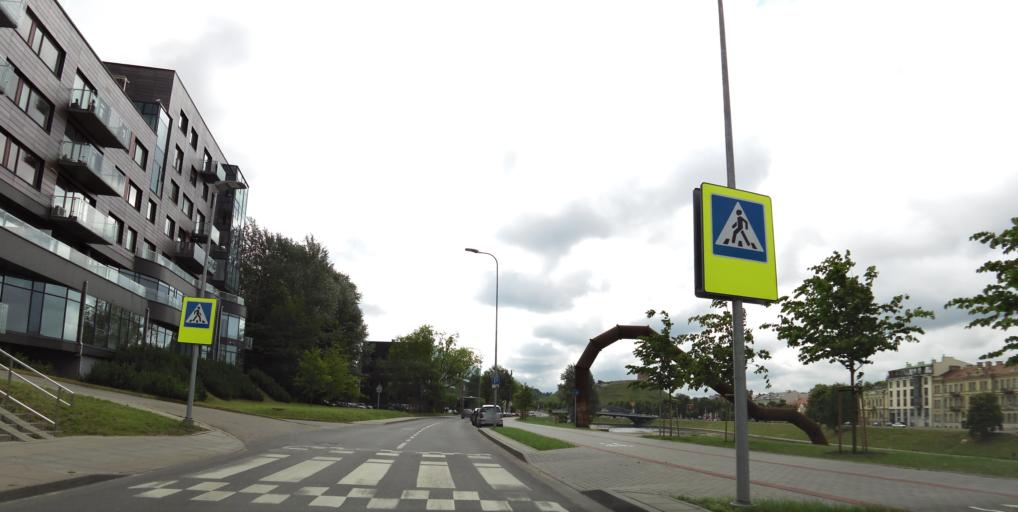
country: LT
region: Vilnius County
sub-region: Vilnius
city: Vilnius
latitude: 54.6915
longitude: 25.2840
